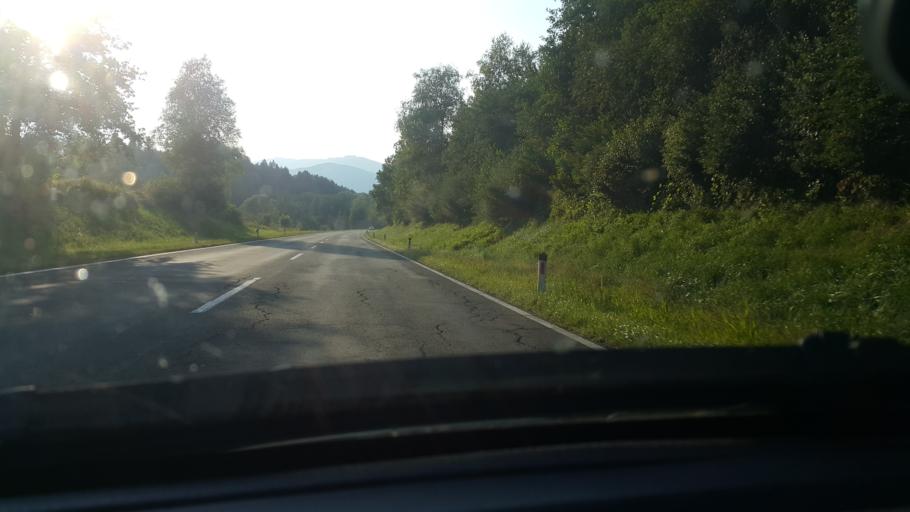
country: AT
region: Carinthia
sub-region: Politischer Bezirk Feldkirchen
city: Feldkirchen in Karnten
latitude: 46.7102
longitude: 14.1136
